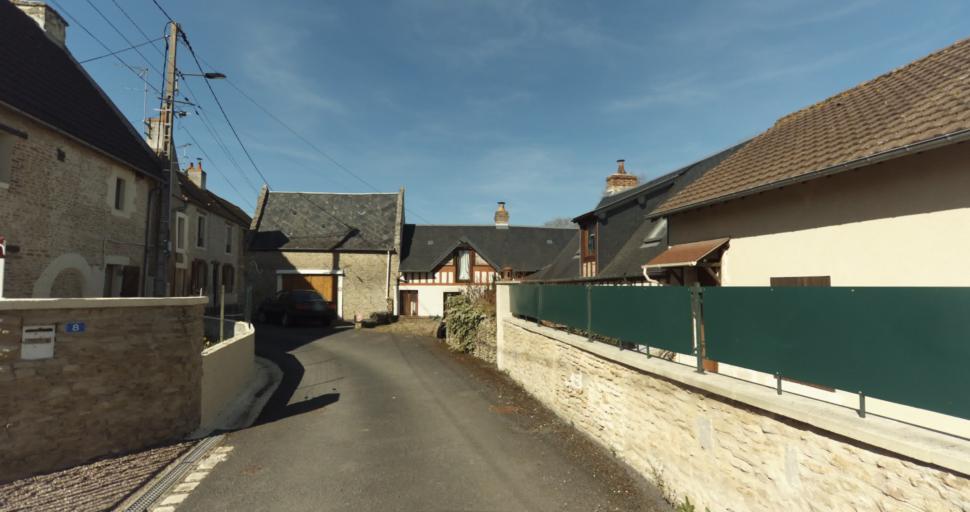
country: FR
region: Lower Normandy
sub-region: Departement du Calvados
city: Saint-Pierre-sur-Dives
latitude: 49.0356
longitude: -0.0257
